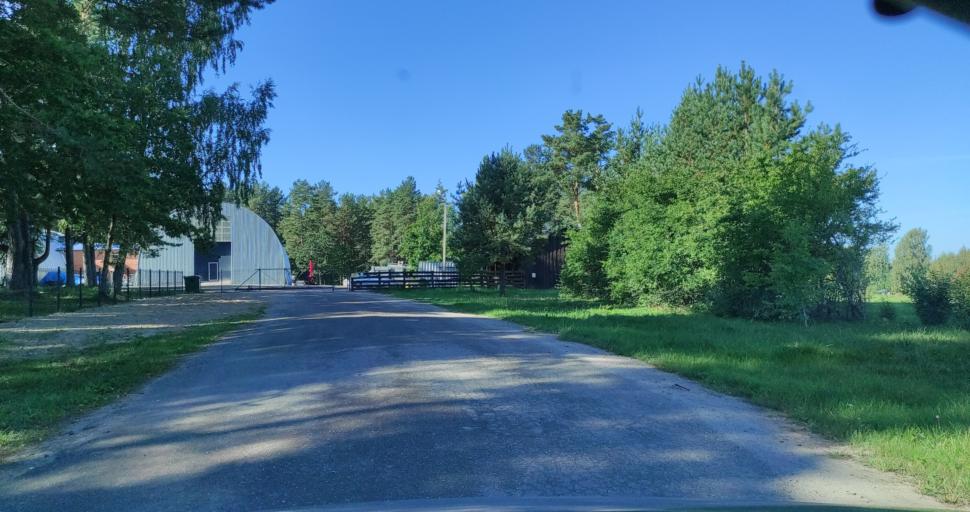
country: LV
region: Kuldigas Rajons
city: Kuldiga
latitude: 56.9712
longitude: 21.9277
